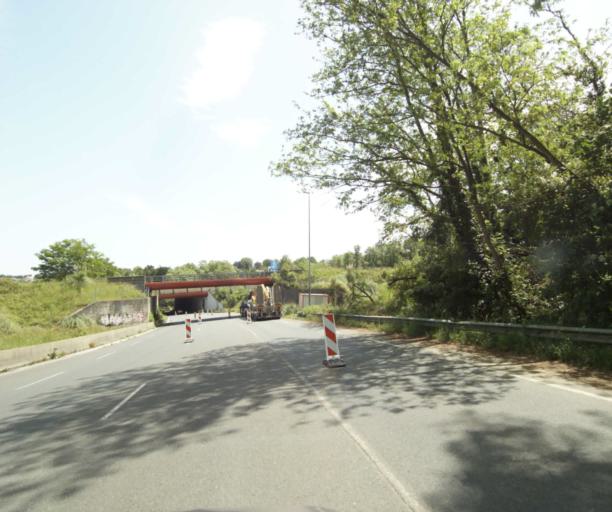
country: FR
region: Aquitaine
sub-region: Departement des Pyrenees-Atlantiques
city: Bayonne
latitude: 43.4767
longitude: -1.4530
